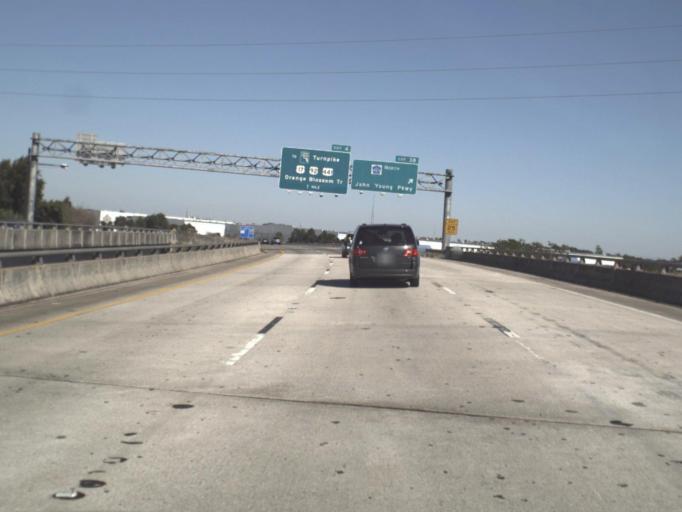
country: US
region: Florida
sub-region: Orange County
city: Williamsburg
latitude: 28.4217
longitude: -81.4232
